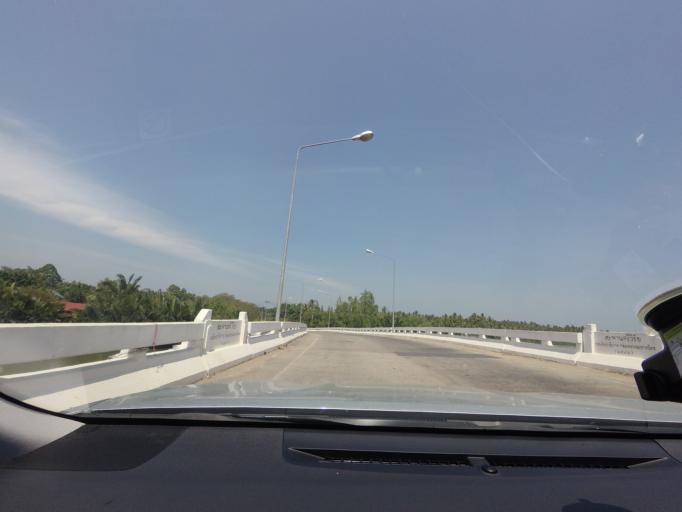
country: TH
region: Surat Thani
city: Phunphin
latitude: 9.1892
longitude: 99.2633
